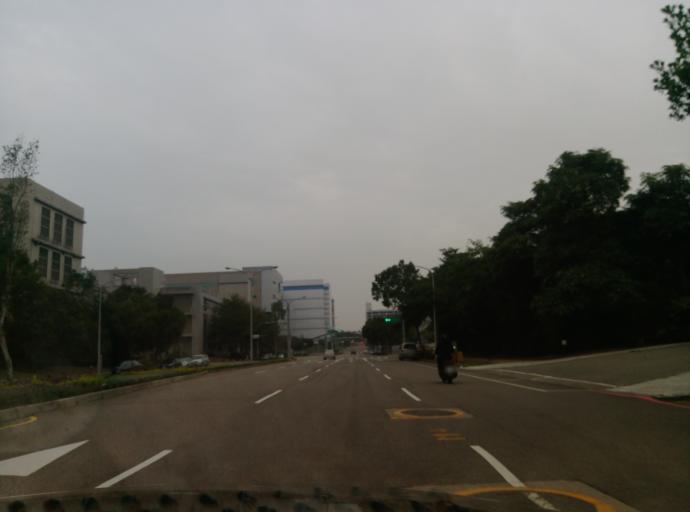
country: TW
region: Taiwan
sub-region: Hsinchu
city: Hsinchu
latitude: 24.7106
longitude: 120.9148
